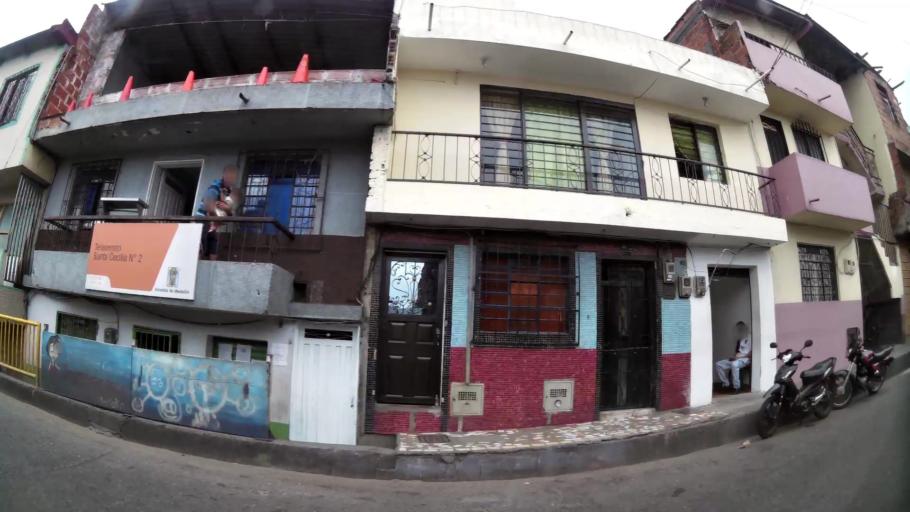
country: CO
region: Antioquia
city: Medellin
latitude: 6.2896
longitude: -75.5534
